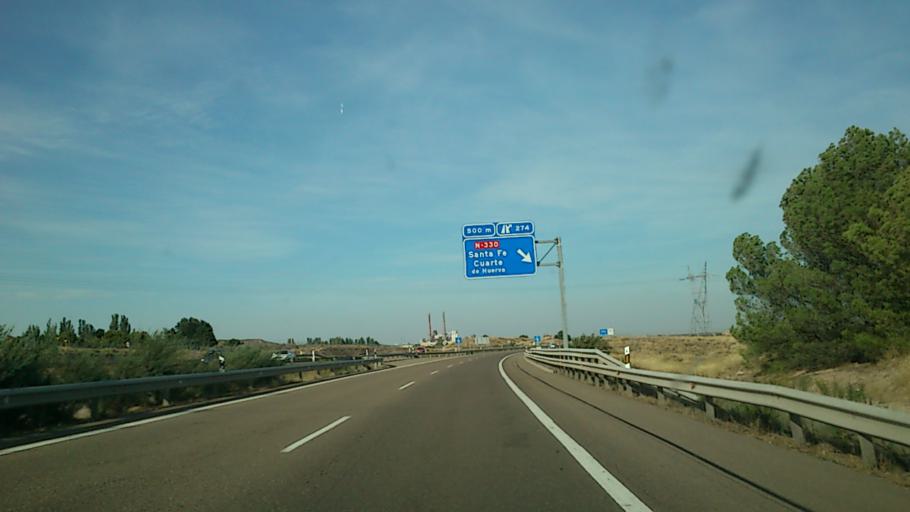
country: ES
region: Aragon
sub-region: Provincia de Zaragoza
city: Cuarte de Huerva
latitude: 41.5862
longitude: -0.9533
